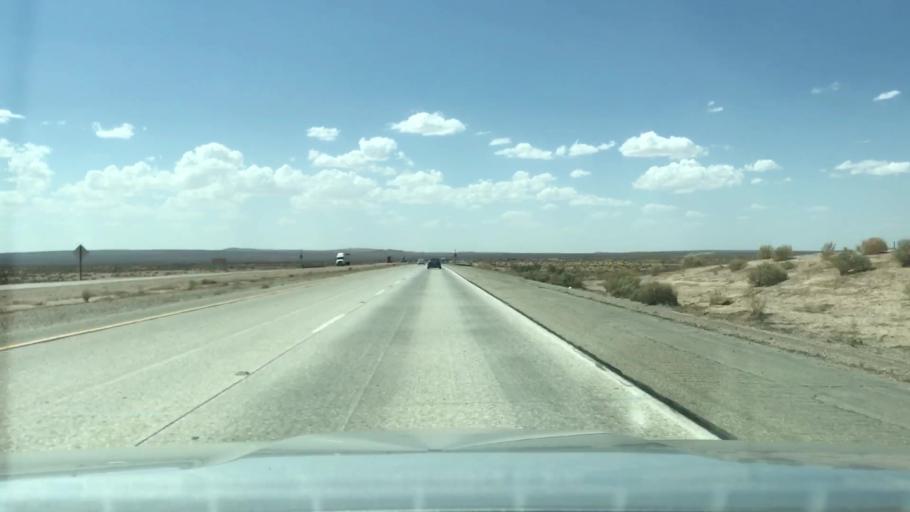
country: US
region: California
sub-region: San Bernardino County
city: Lenwood
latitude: 34.9248
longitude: -117.3331
